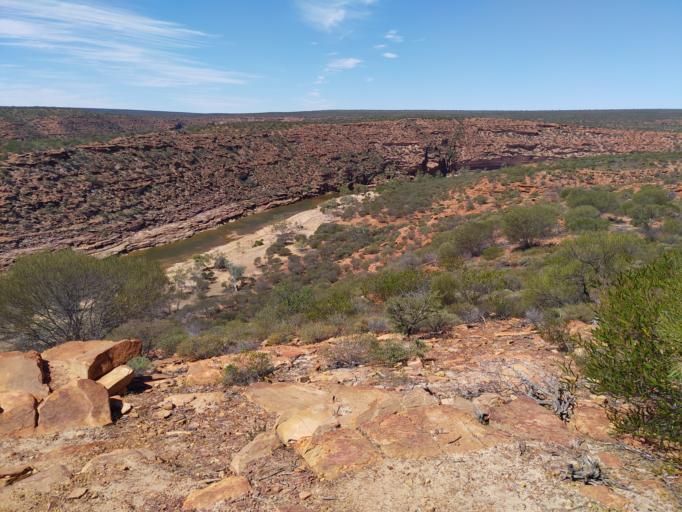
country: AU
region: Western Australia
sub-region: Northampton Shire
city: Kalbarri
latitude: -27.5575
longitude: 114.4452
